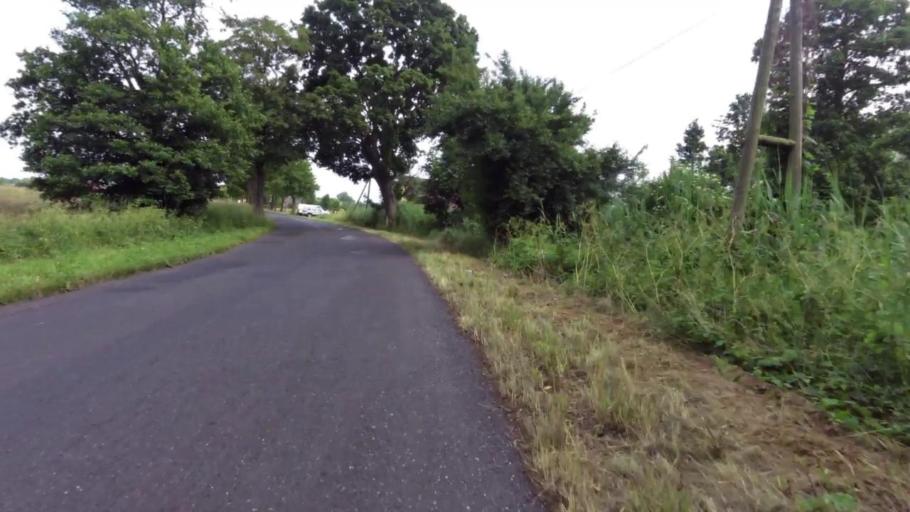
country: PL
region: West Pomeranian Voivodeship
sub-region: Powiat goleniowski
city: Stepnica
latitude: 53.6615
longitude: 14.6029
